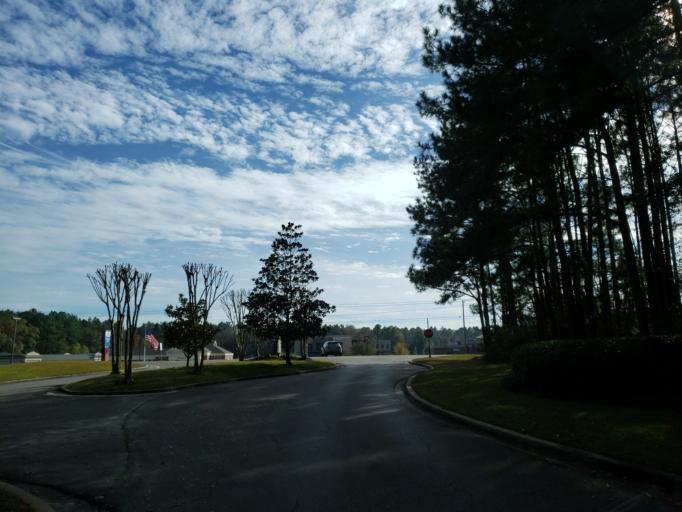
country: US
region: Mississippi
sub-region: Lamar County
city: West Hattiesburg
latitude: 31.3138
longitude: -89.4694
